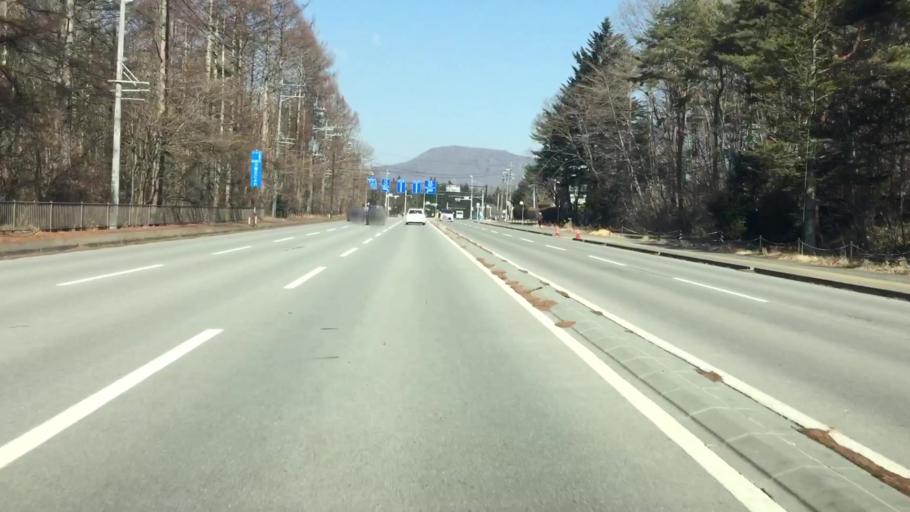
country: JP
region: Nagano
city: Saku
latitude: 36.3219
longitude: 138.6295
